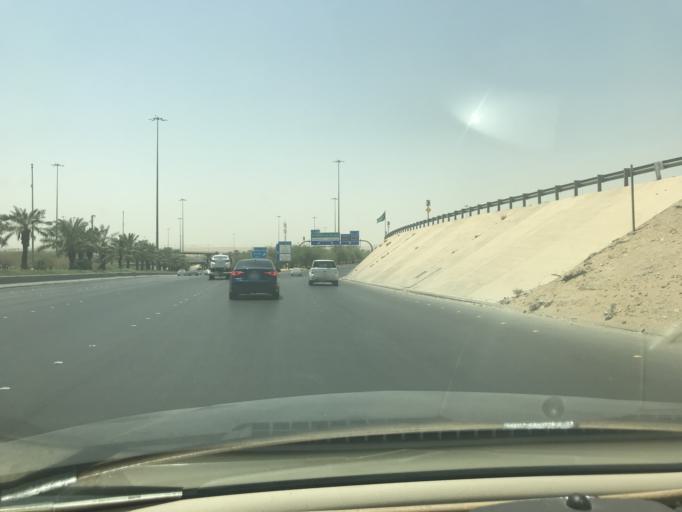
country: SA
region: Ar Riyad
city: Riyadh
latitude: 24.7393
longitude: 46.5944
